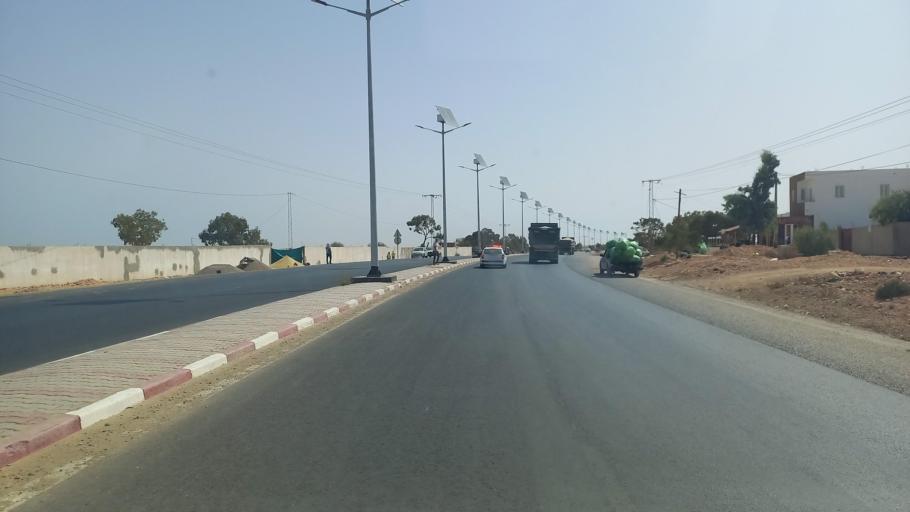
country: TN
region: Madanin
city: Medenine
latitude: 33.3604
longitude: 10.5560
